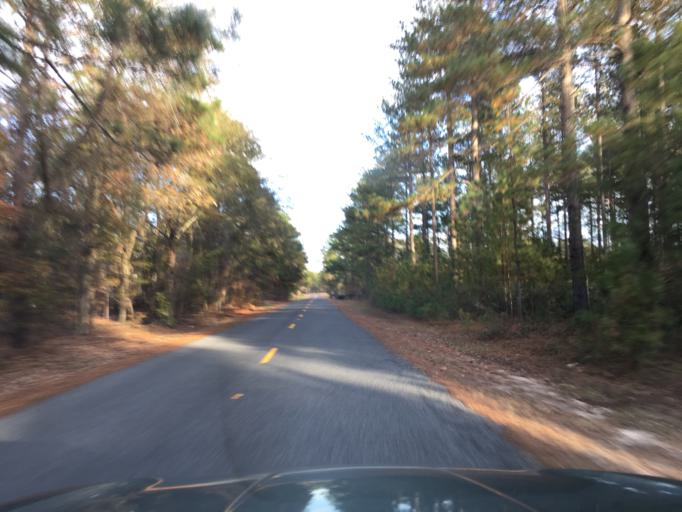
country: US
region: South Carolina
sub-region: Lexington County
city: Leesville
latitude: 33.6852
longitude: -81.3695
